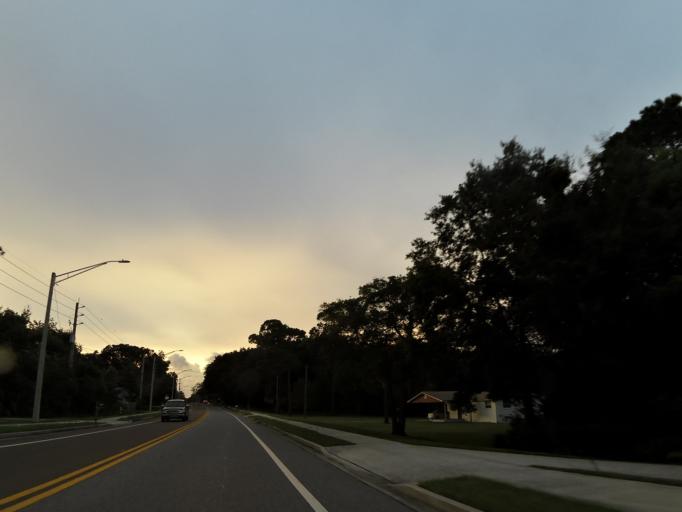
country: US
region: Florida
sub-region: Duval County
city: Jacksonville
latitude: 30.3577
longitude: -81.5484
